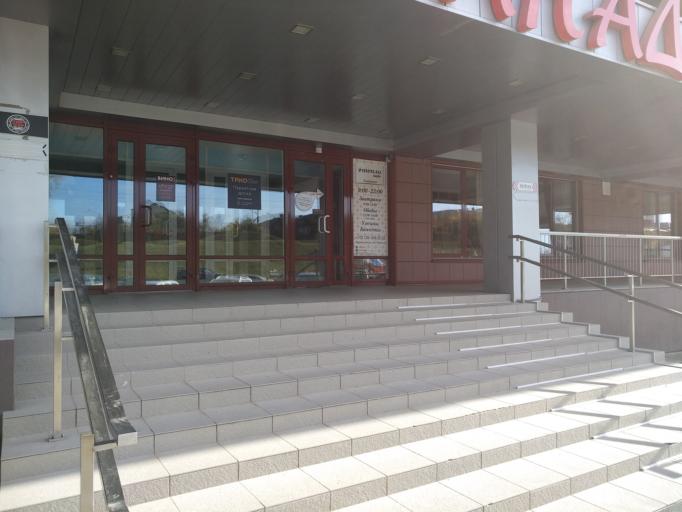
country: BY
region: Minsk
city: Minsk
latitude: 53.9386
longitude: 27.5845
